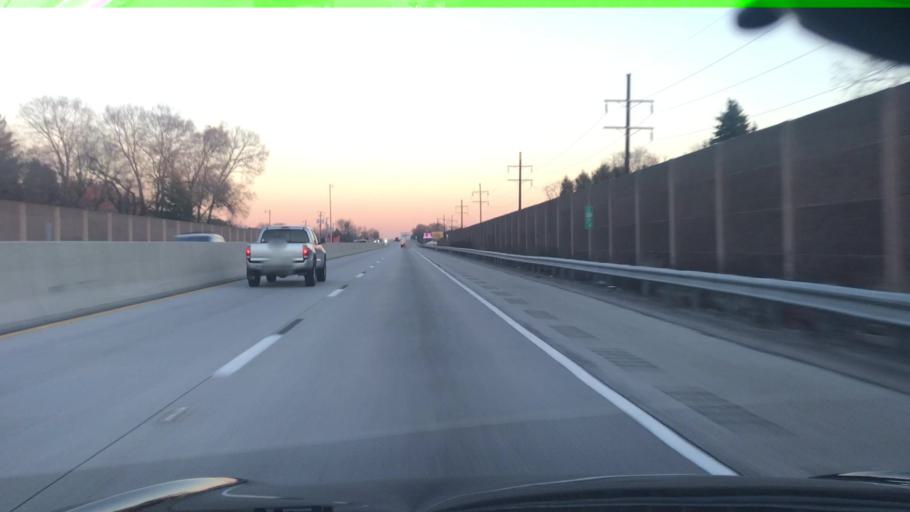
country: US
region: Pennsylvania
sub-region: Cumberland County
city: Shiremanstown
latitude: 40.2336
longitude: -76.9616
